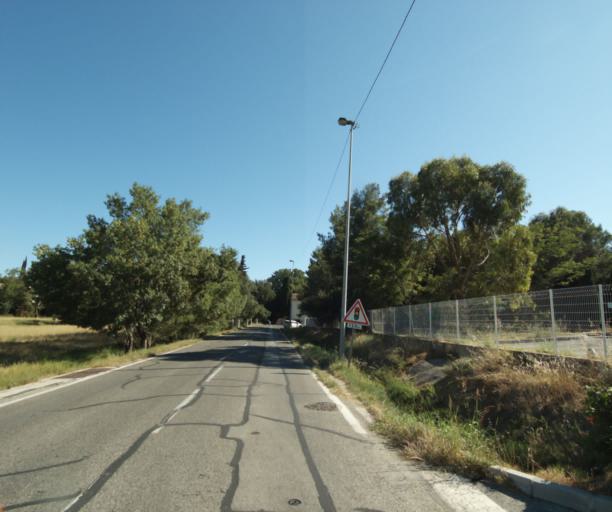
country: FR
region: Provence-Alpes-Cote d'Azur
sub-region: Departement du Var
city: La Garde
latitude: 43.1109
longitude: 6.0009
